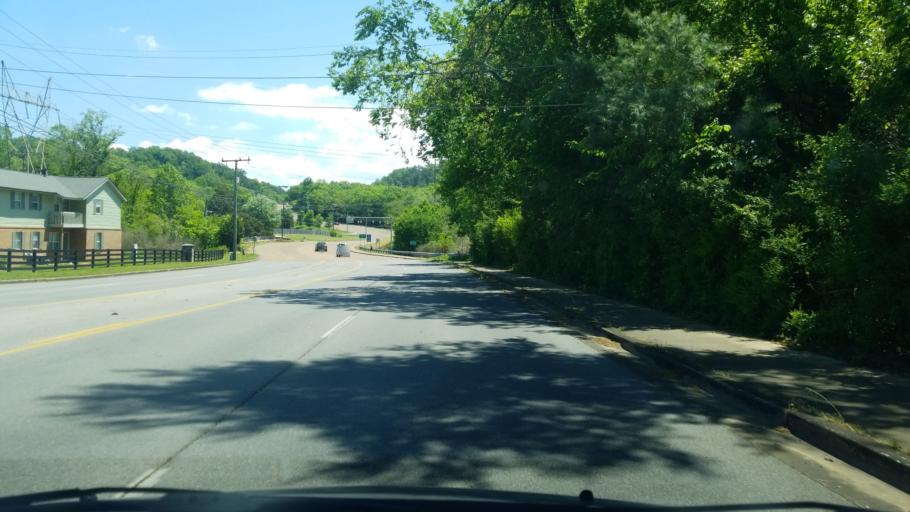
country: US
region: Tennessee
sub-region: Hamilton County
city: Red Bank
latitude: 35.1260
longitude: -85.3088
